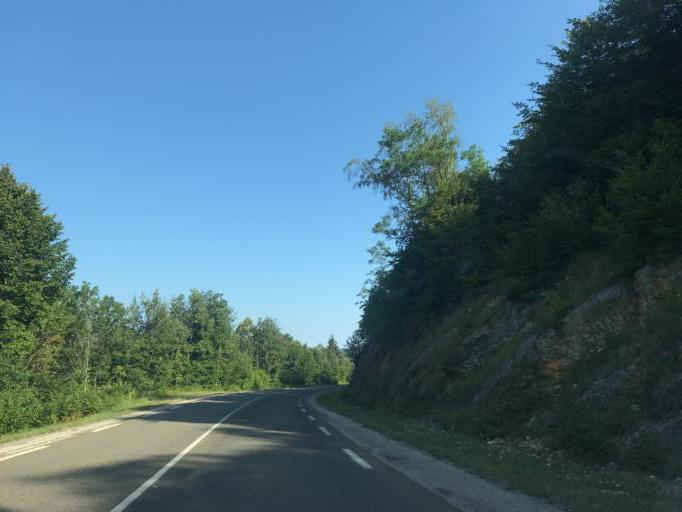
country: FR
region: Franche-Comte
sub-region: Departement du Jura
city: Moirans-en-Montagne
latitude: 46.3973
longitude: 5.7350
